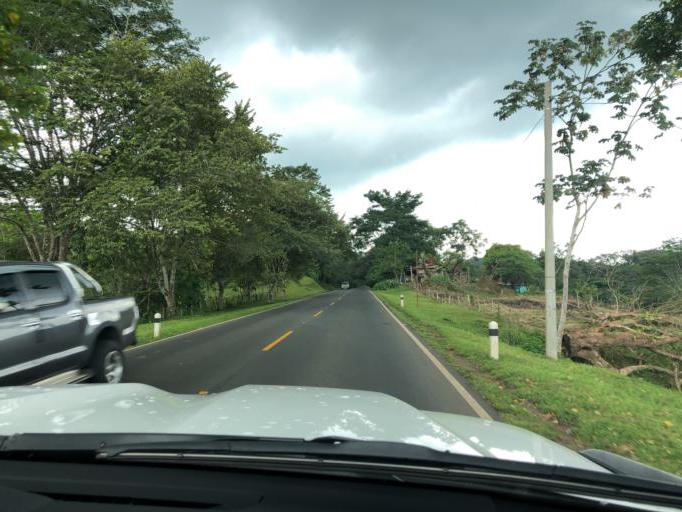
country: NI
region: Chontales
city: Villa Sandino
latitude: 11.9905
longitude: -84.8197
